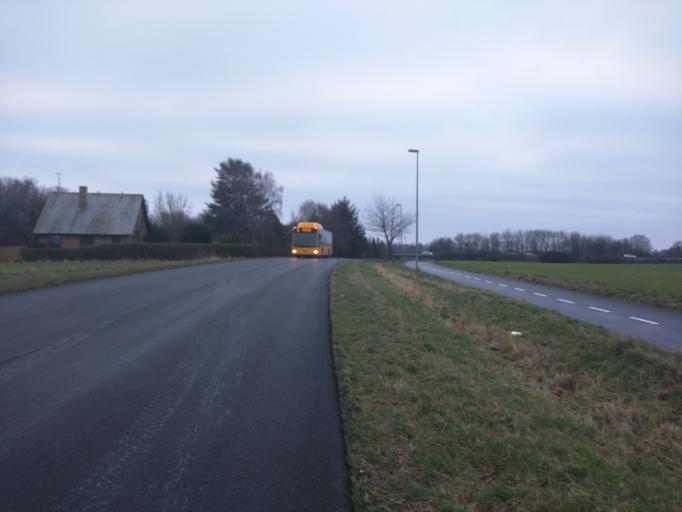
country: DK
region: South Denmark
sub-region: Fredericia Kommune
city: Snoghoj
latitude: 55.5257
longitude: 9.7321
